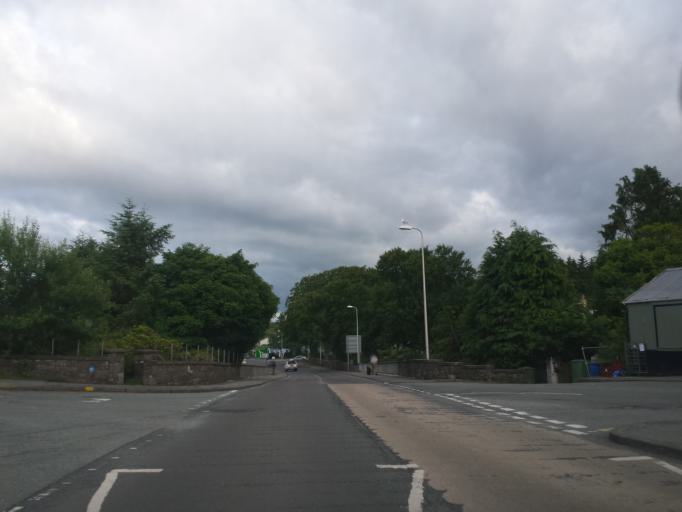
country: GB
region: Scotland
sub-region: Highland
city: Portree
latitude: 57.2428
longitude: -5.9132
